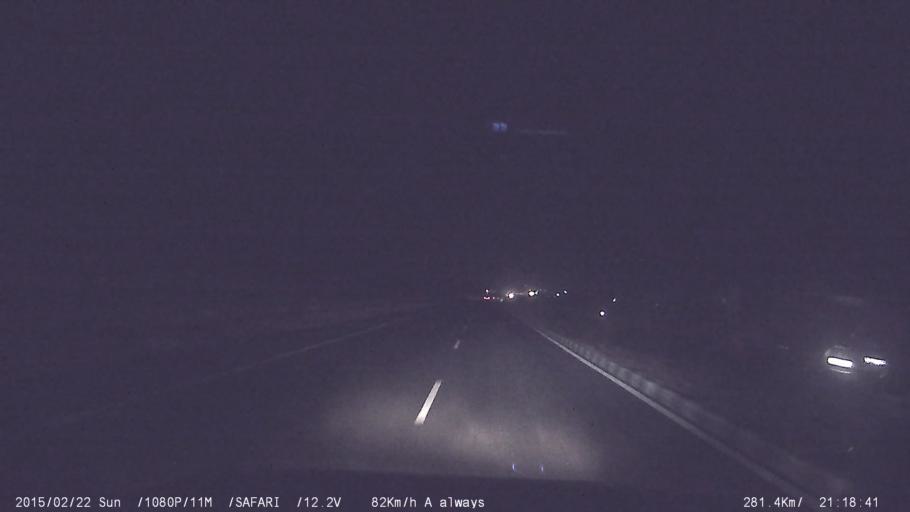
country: IN
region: Tamil Nadu
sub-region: Karur
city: Pallappatti
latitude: 10.8404
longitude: 77.9666
